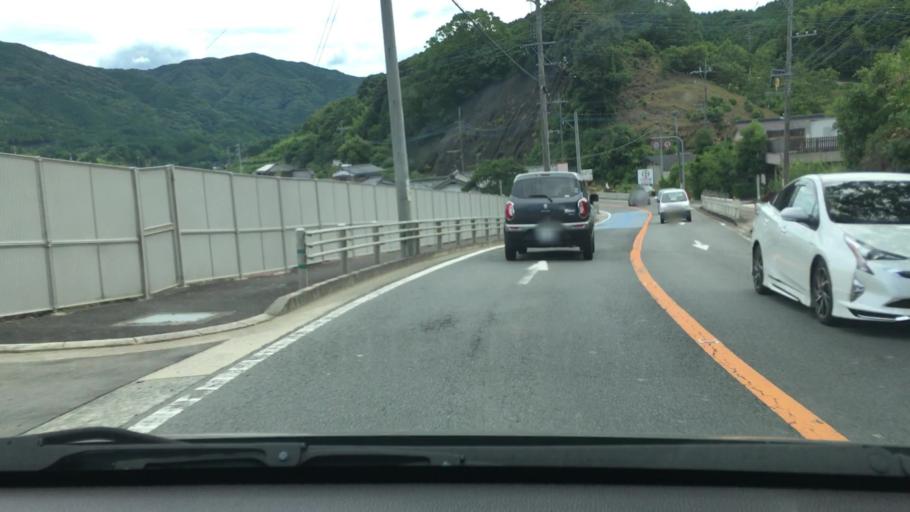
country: JP
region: Nagasaki
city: Sasebo
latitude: 32.9908
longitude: 129.7380
